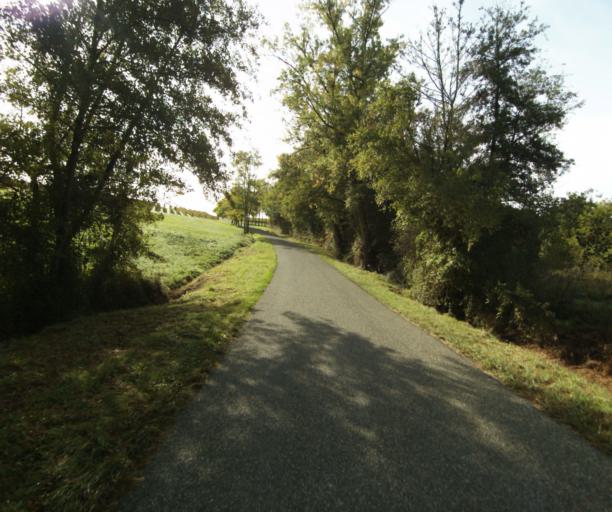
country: FR
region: Midi-Pyrenees
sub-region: Departement du Gers
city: Eauze
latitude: 43.9293
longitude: 0.1238
